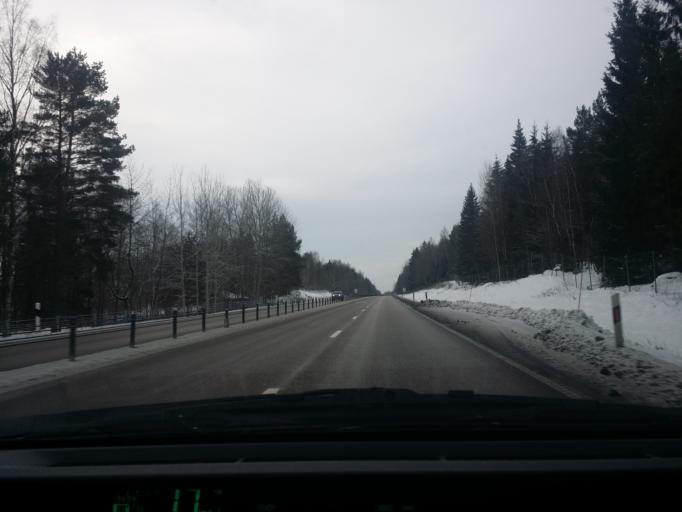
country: SE
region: Vaestra Goetaland
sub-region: Mariestads Kommun
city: Mariestad
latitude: 58.6099
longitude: 13.8043
